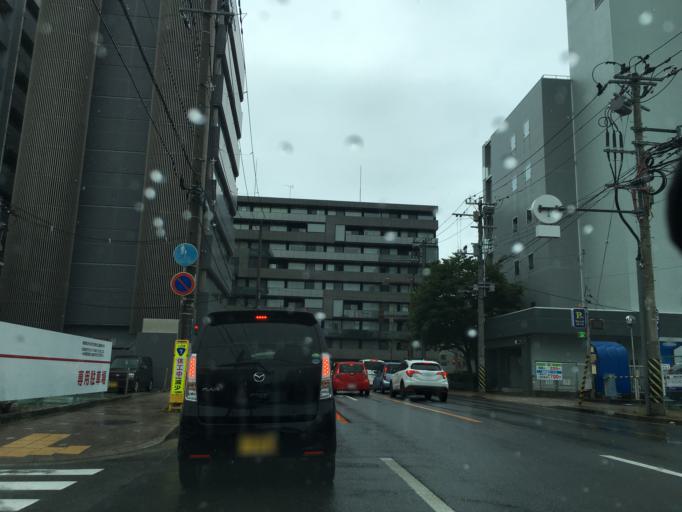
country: JP
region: Niigata
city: Niigata-shi
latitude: 37.9160
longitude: 139.0653
